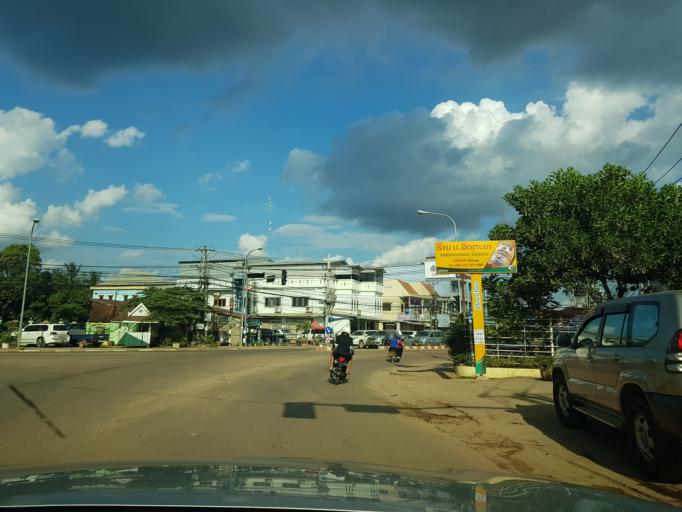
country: TH
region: Nong Khai
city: Si Chiang Mai
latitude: 17.9746
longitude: 102.5573
